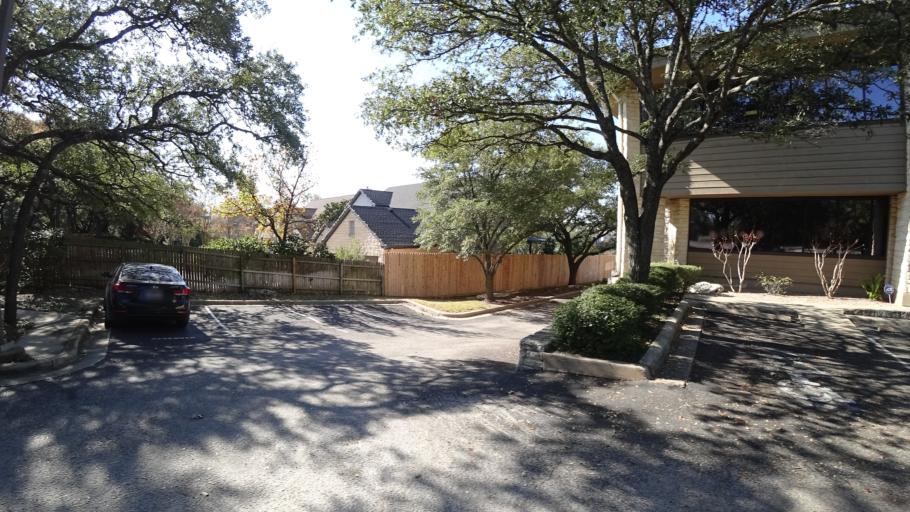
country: US
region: Texas
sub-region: Williamson County
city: Jollyville
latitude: 30.3786
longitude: -97.7653
